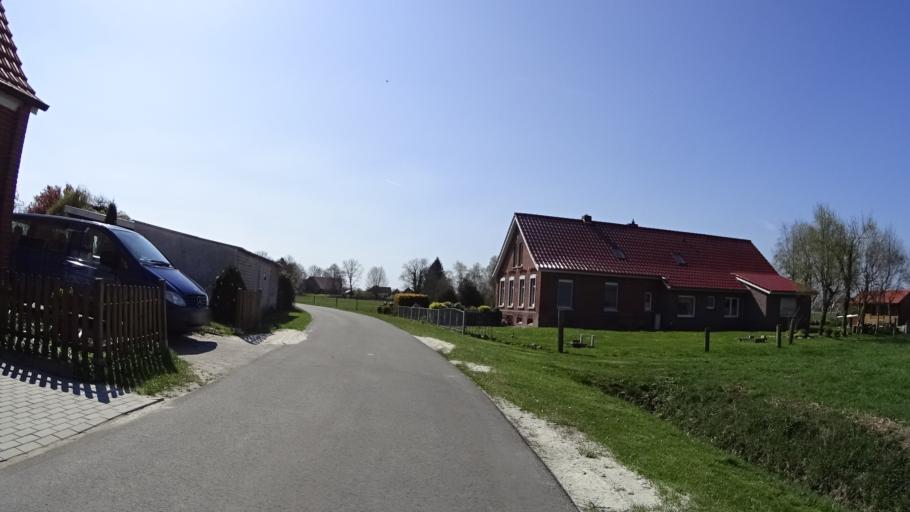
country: DE
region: Lower Saxony
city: Leer
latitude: 53.2027
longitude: 7.4035
